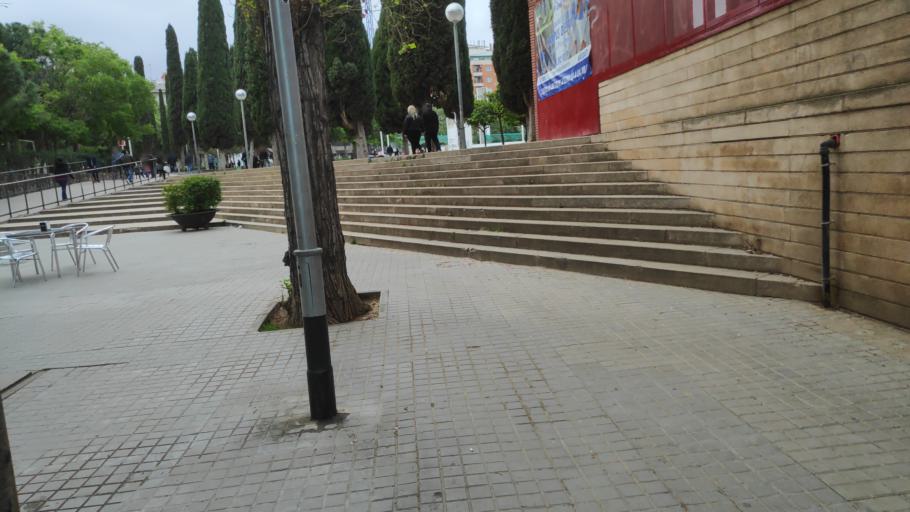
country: ES
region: Catalonia
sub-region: Provincia de Barcelona
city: Sant Marti
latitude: 41.4072
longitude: 2.1909
